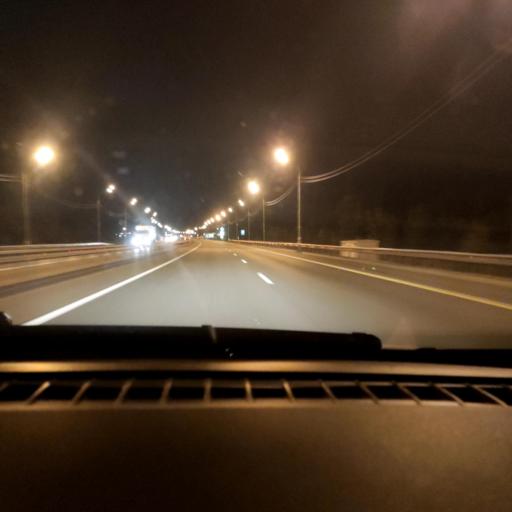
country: RU
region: Lipetsk
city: Khlevnoye
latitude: 52.2674
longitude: 39.0590
